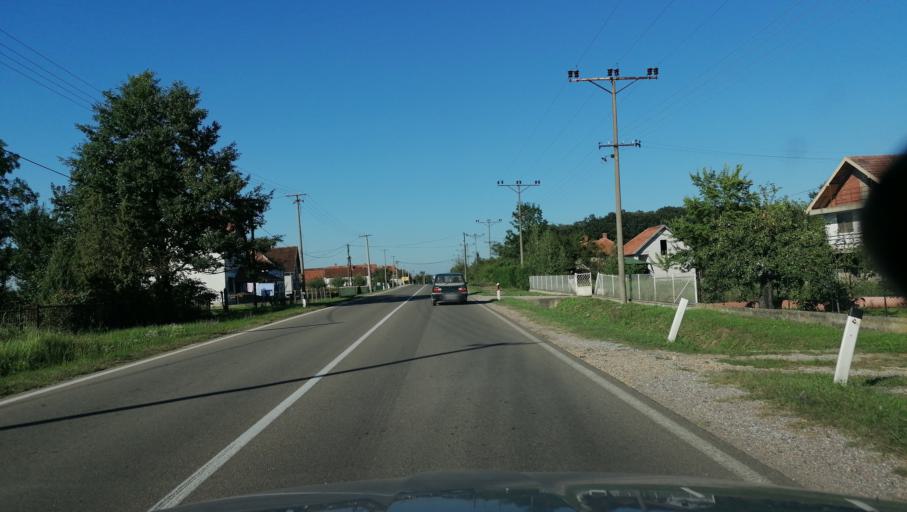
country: RS
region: Central Serbia
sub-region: Sumadijski Okrug
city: Knic
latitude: 43.9069
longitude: 20.6347
